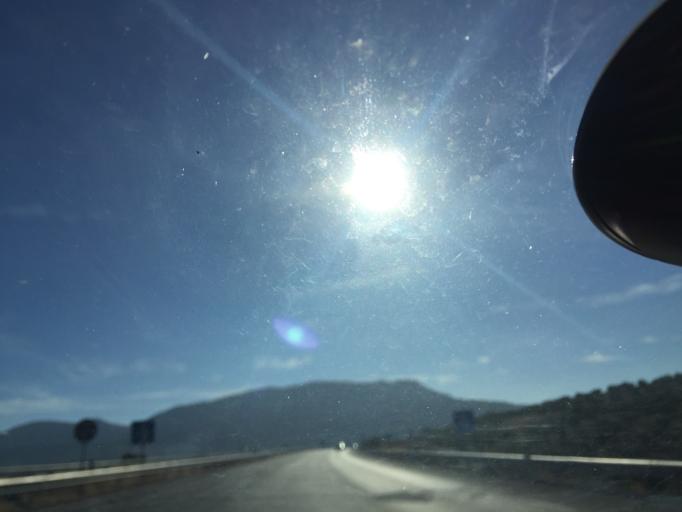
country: ES
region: Andalusia
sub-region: Provincia de Jaen
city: La Guardia de Jaen
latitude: 37.7596
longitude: -3.7080
